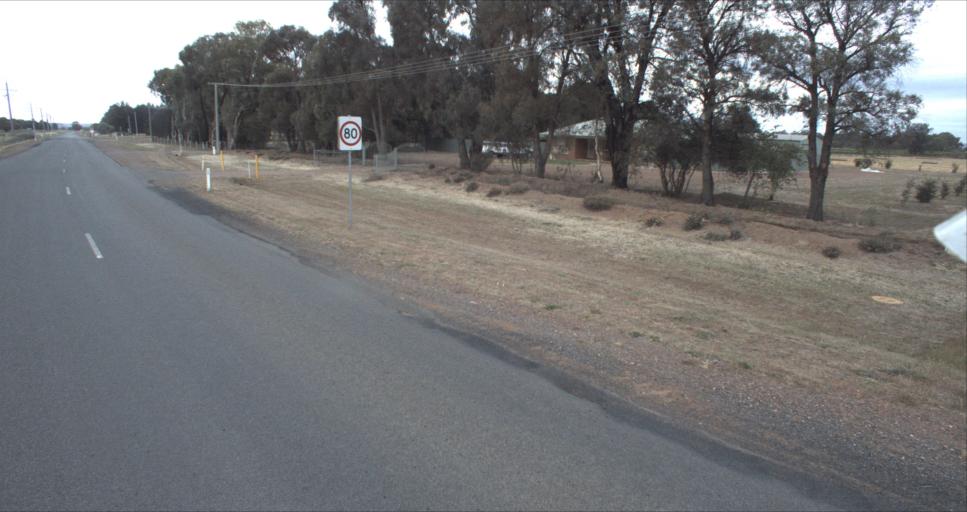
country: AU
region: New South Wales
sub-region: Leeton
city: Leeton
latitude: -34.5335
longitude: 146.3883
